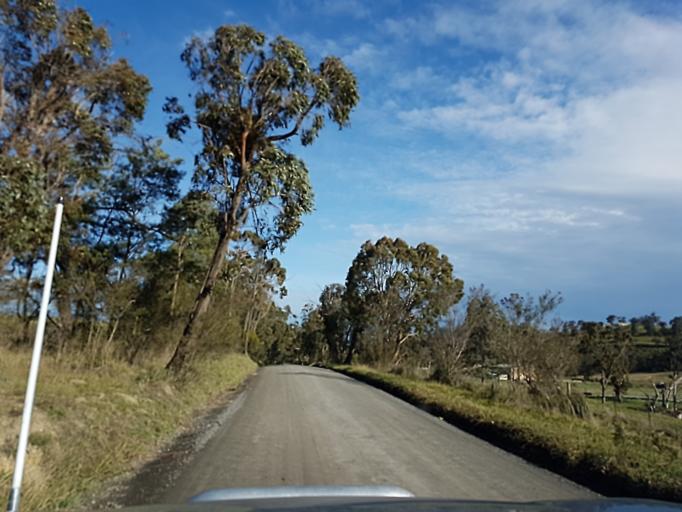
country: AU
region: Victoria
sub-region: Yarra Ranges
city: Healesville
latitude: -37.6472
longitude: 145.4709
